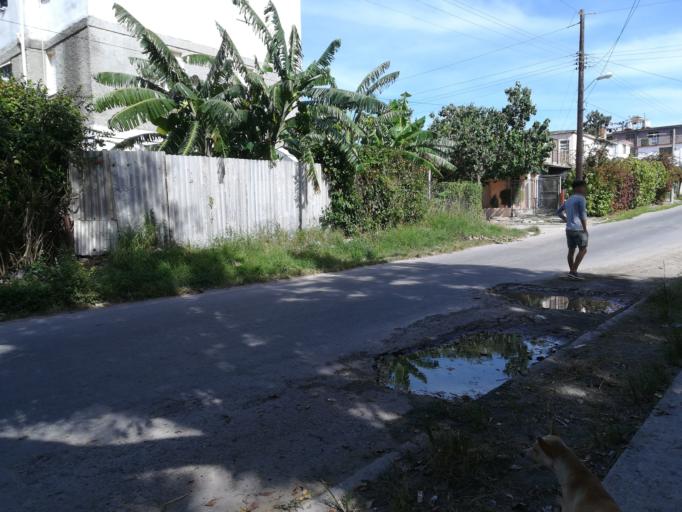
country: CU
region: La Habana
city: Guanabacoa
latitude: 23.1154
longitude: -82.3003
